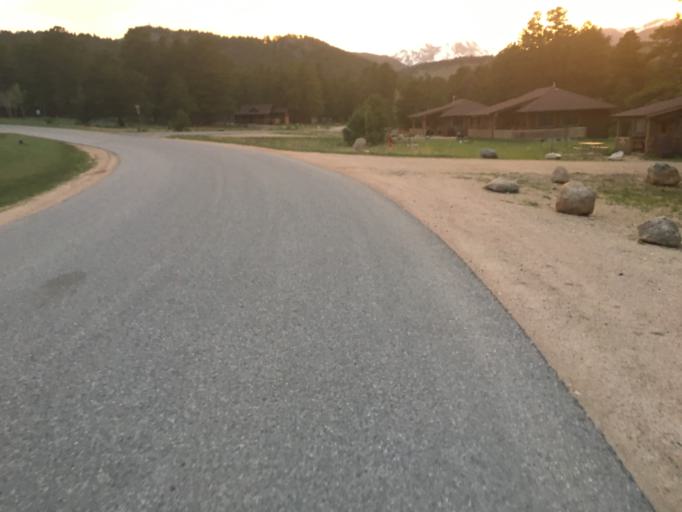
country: US
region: Colorado
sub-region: Larimer County
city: Estes Park
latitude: 40.3427
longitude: -105.5724
